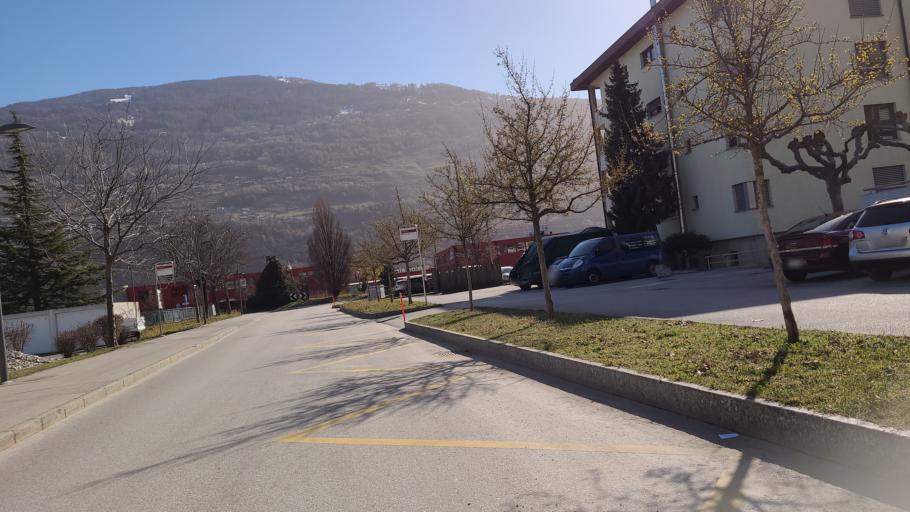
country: CH
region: Valais
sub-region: Sion District
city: Sitten
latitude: 46.2239
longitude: 7.3374
